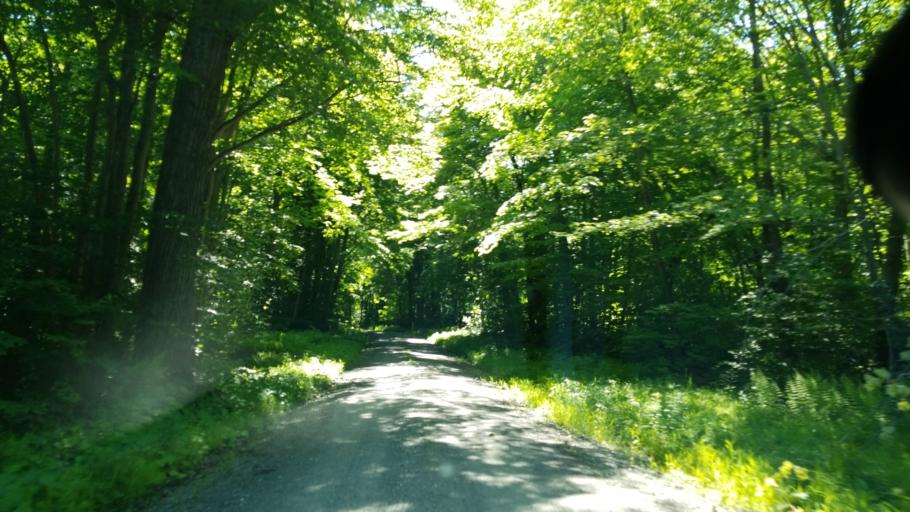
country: US
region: Pennsylvania
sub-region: Clearfield County
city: Clearfield
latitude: 41.2116
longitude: -78.3959
